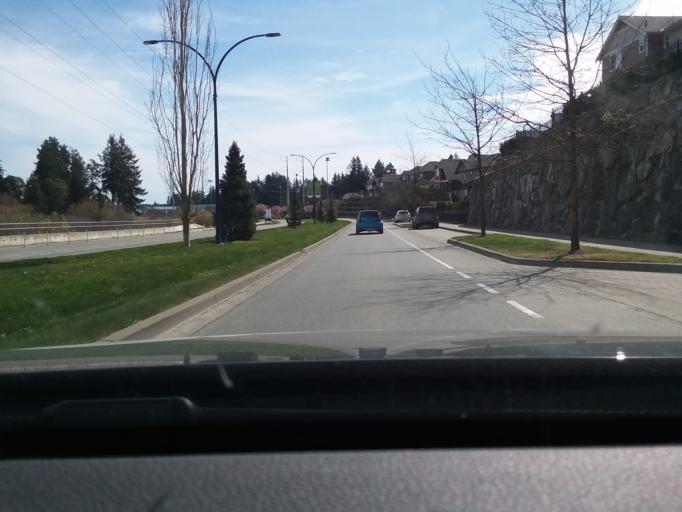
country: CA
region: British Columbia
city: Langford
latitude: 48.4449
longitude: -123.5307
